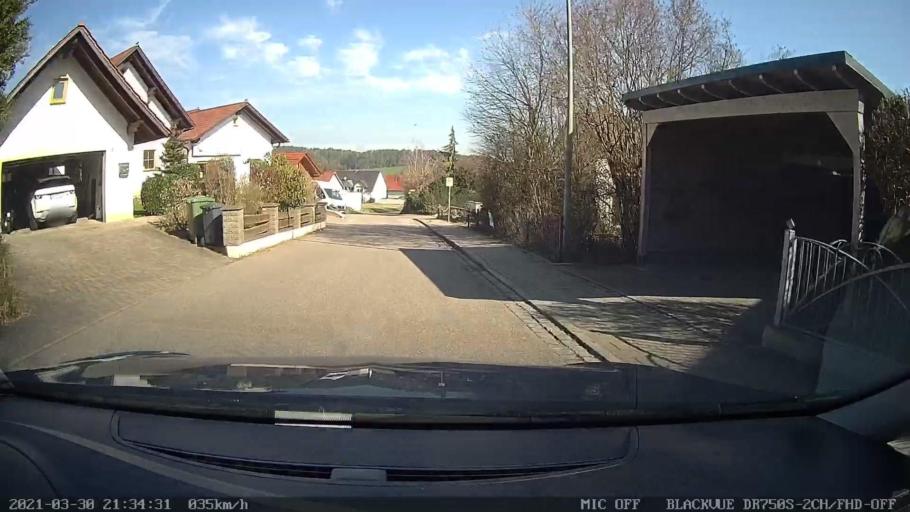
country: DE
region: Bavaria
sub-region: Upper Palatinate
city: Zeitlarn
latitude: 49.0977
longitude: 12.1000
